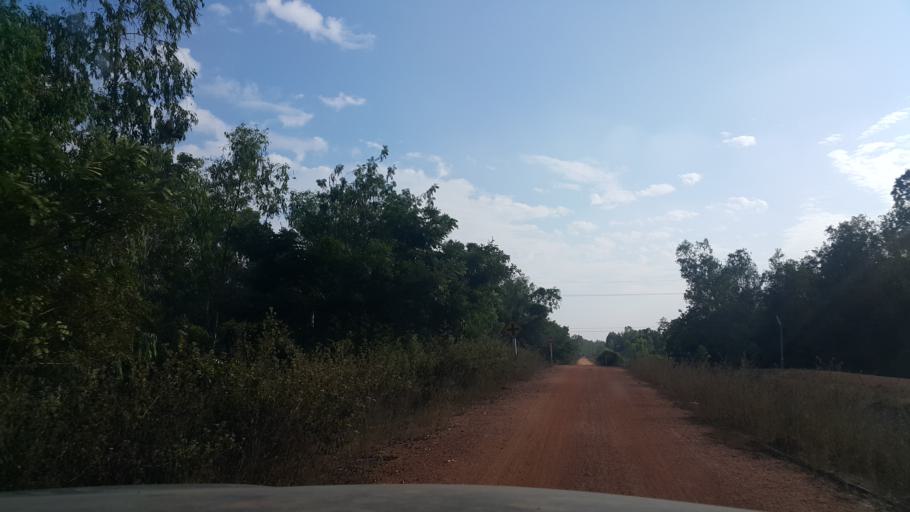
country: TH
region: Lampang
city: Hang Chat
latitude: 18.2710
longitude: 99.3720
